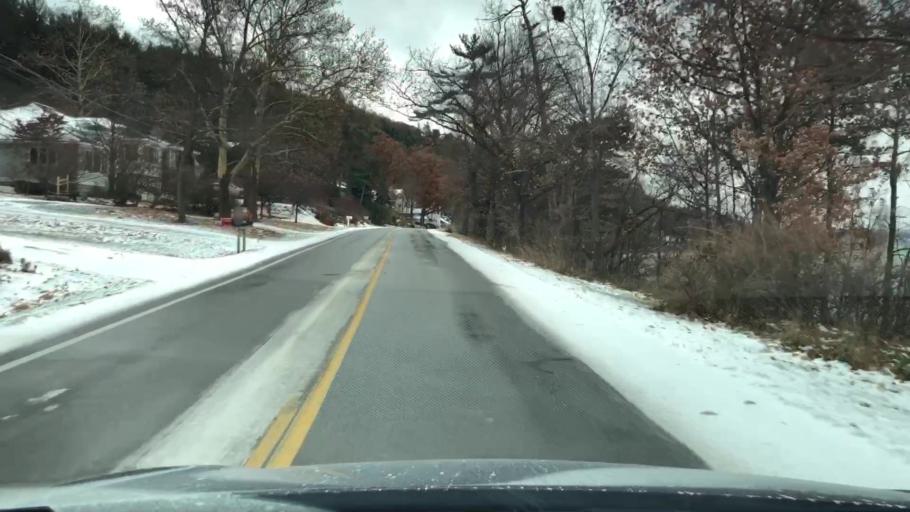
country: US
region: Michigan
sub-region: Grand Traverse County
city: Traverse City
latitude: 44.8042
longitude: -85.5813
